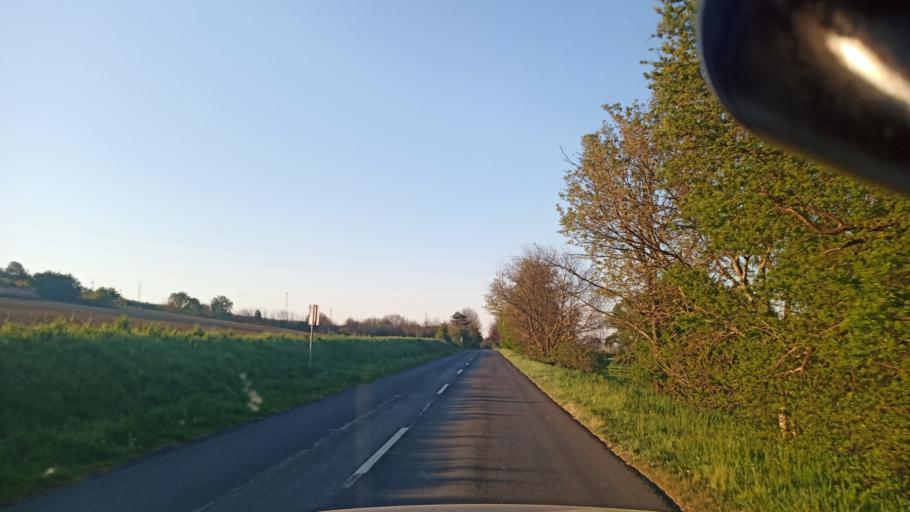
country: HU
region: Zala
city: Heviz
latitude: 46.7942
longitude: 17.1254
